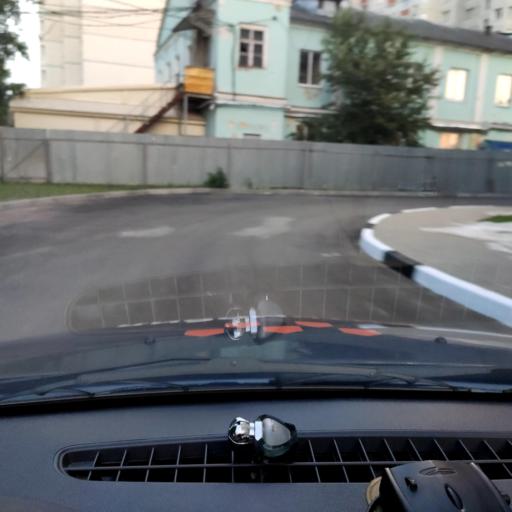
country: RU
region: Voronezj
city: Voronezh
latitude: 51.6447
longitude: 39.1635
